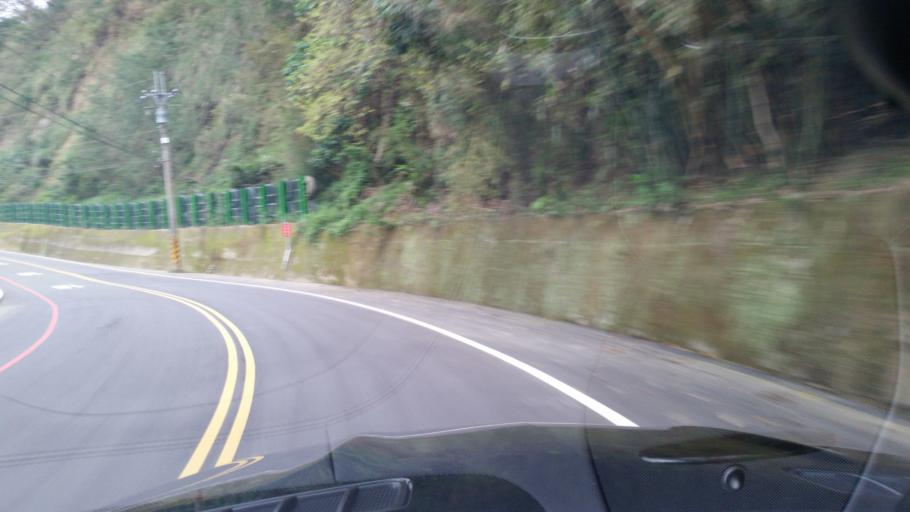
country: TW
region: Taiwan
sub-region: Miaoli
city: Miaoli
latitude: 24.5797
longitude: 120.8840
